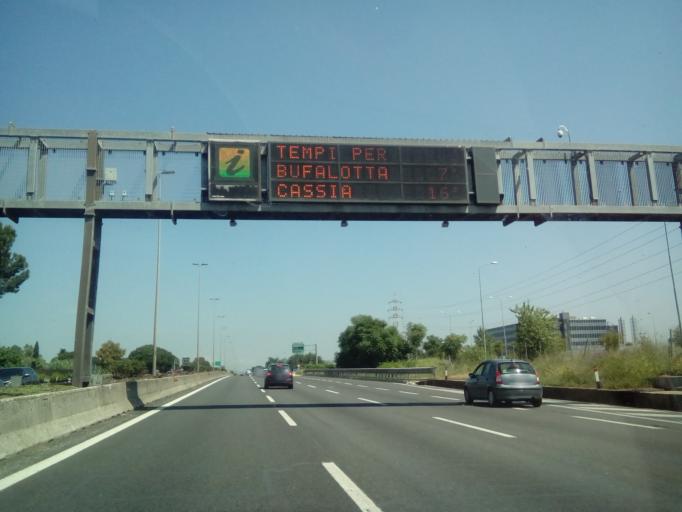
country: IT
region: Latium
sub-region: Citta metropolitana di Roma Capitale
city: Setteville
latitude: 41.9070
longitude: 12.6156
